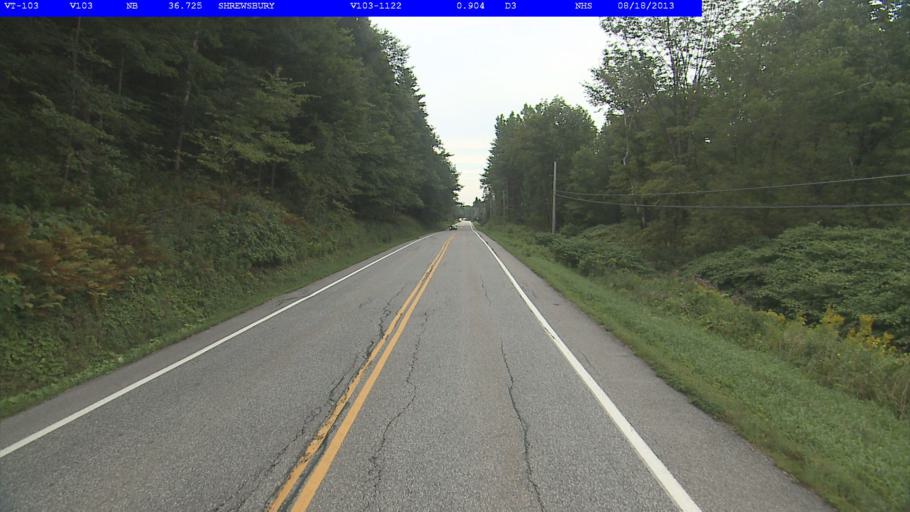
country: US
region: Vermont
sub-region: Rutland County
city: Rutland
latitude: 43.4867
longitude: -72.8939
